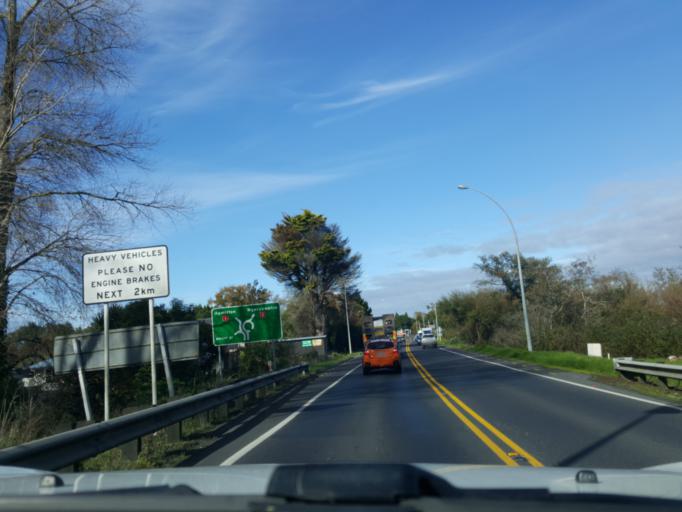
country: NZ
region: Waikato
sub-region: Waikato District
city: Ngaruawahia
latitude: -37.6092
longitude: 175.1852
